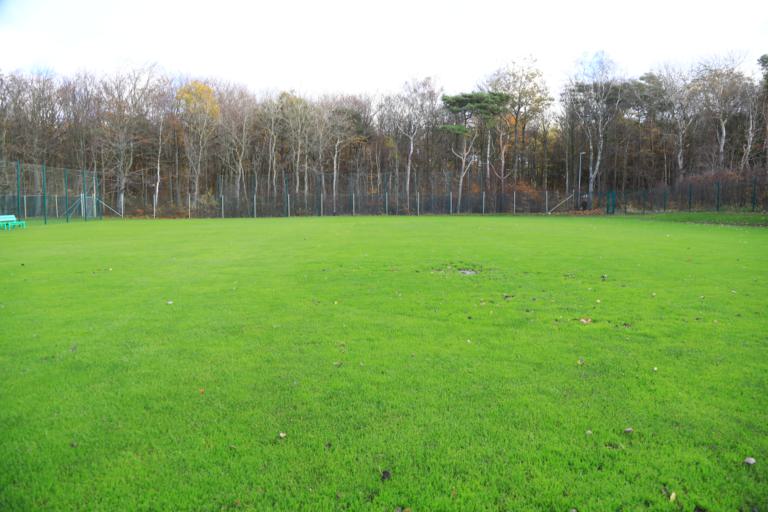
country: SE
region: Halland
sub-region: Varbergs Kommun
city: Varberg
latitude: 57.0969
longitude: 12.2664
